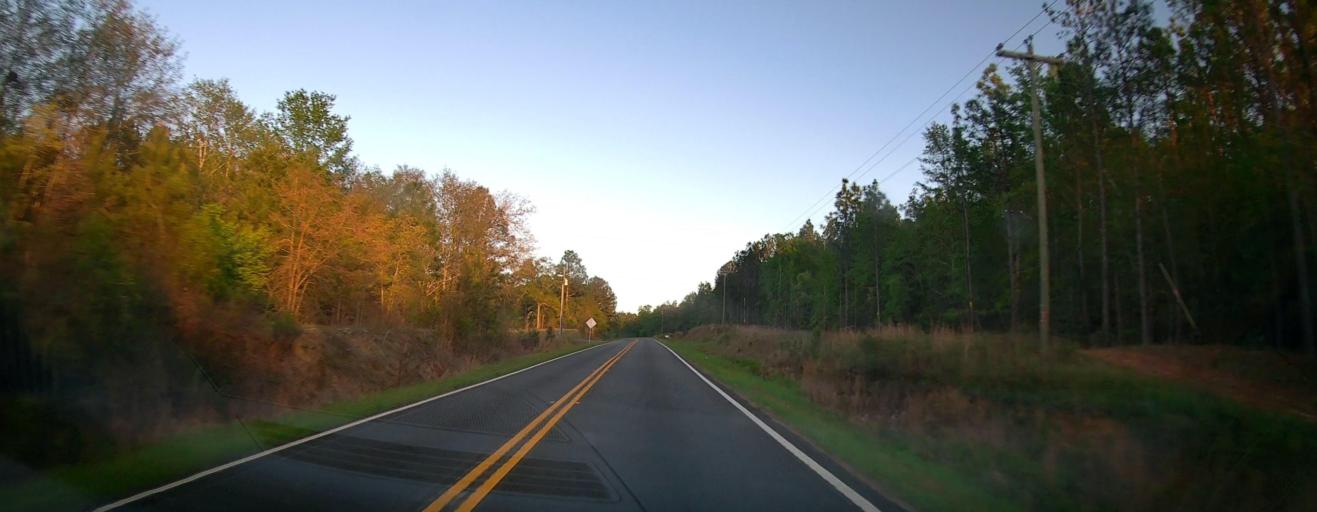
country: US
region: Georgia
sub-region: Marion County
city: Buena Vista
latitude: 32.4444
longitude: -84.6219
